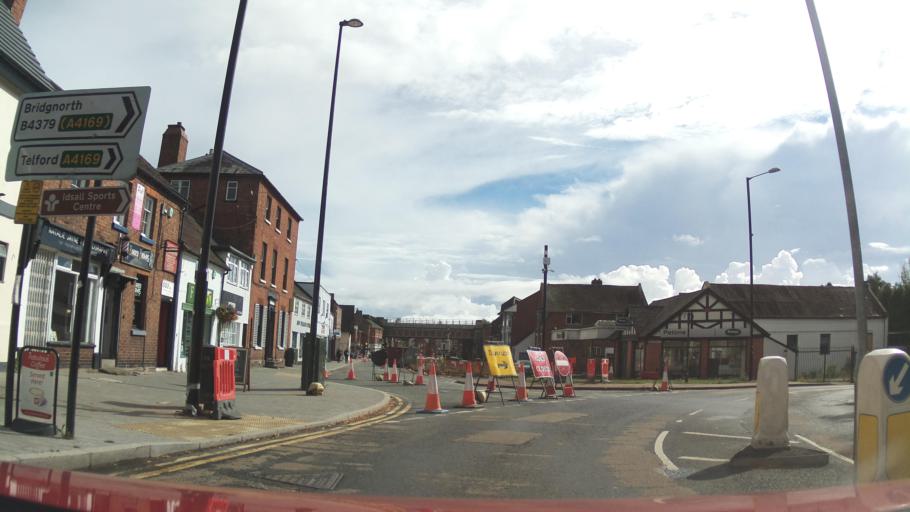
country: GB
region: England
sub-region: Shropshire
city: Shifnal
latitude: 52.6680
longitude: -2.3730
